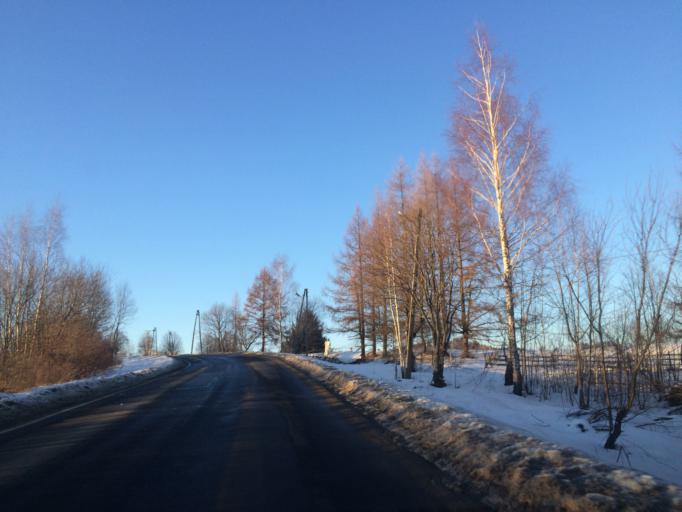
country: PL
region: Subcarpathian Voivodeship
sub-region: Powiat bieszczadzki
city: Lutowiska
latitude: 49.2589
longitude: 22.6843
